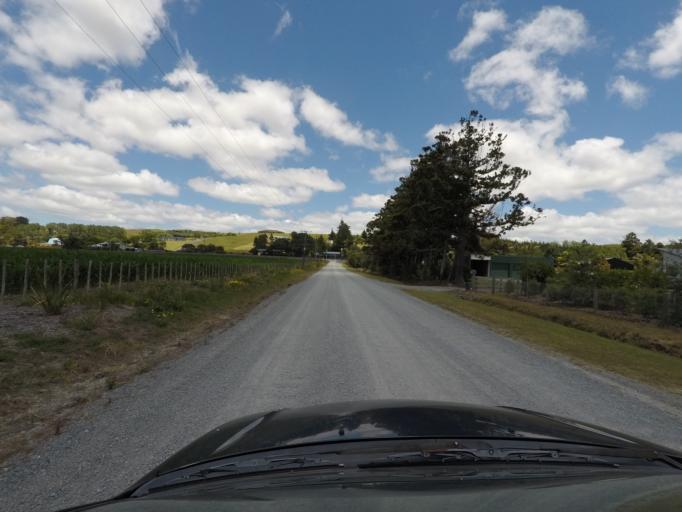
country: NZ
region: Northland
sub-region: Whangarei
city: Ruakaka
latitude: -35.9993
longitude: 174.4766
